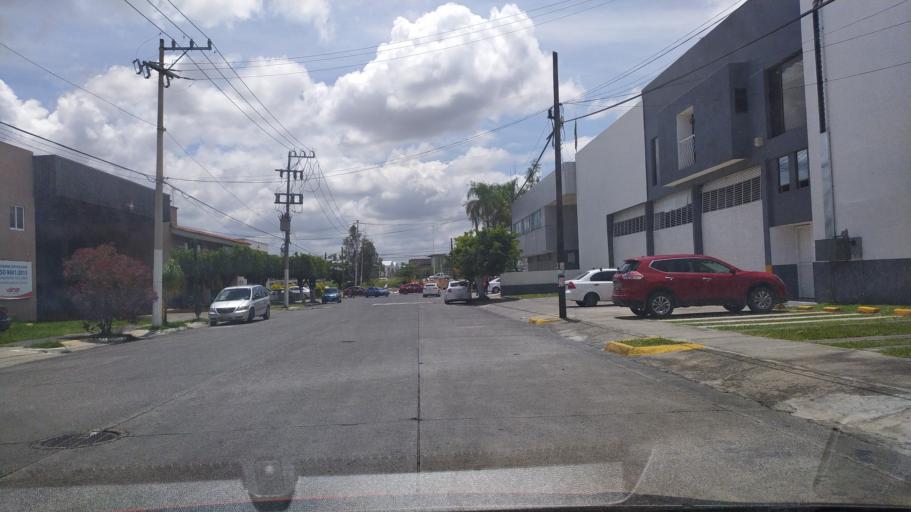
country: MX
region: Jalisco
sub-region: Zapopan
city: Zapopan
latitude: 20.7418
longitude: -103.3885
